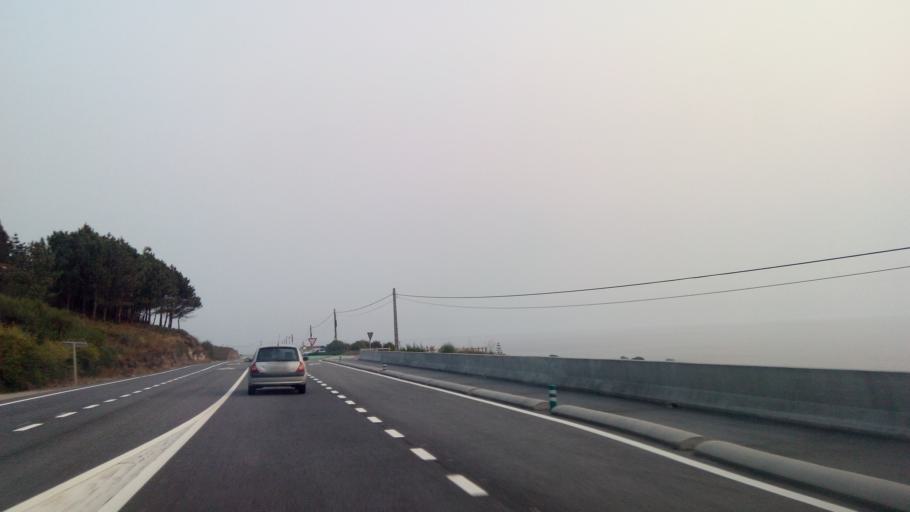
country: ES
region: Galicia
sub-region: Provincia de Pontevedra
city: Baiona
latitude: 42.0713
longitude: -8.8925
